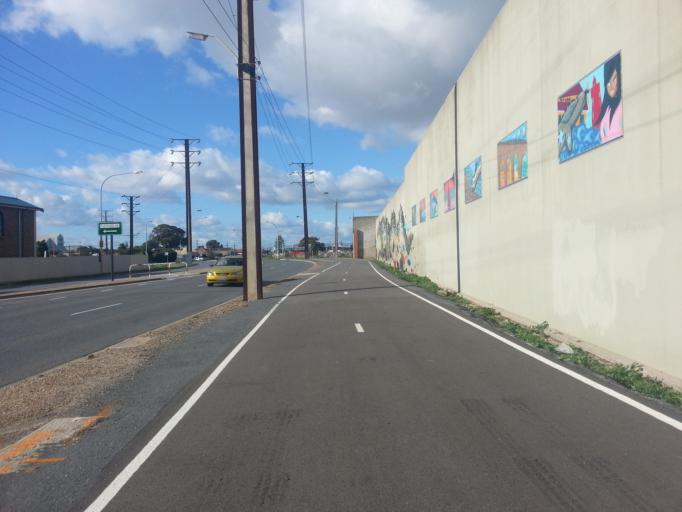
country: AU
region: South Australia
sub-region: Port Adelaide Enfield
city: Birkenhead
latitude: -34.8403
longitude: 138.4970
